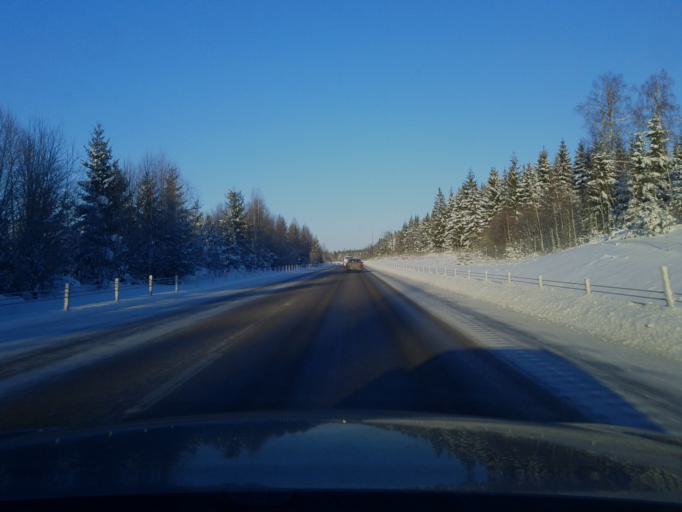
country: SE
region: Uppsala
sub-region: Tierps Kommun
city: Tierp
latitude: 60.3930
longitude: 17.4766
